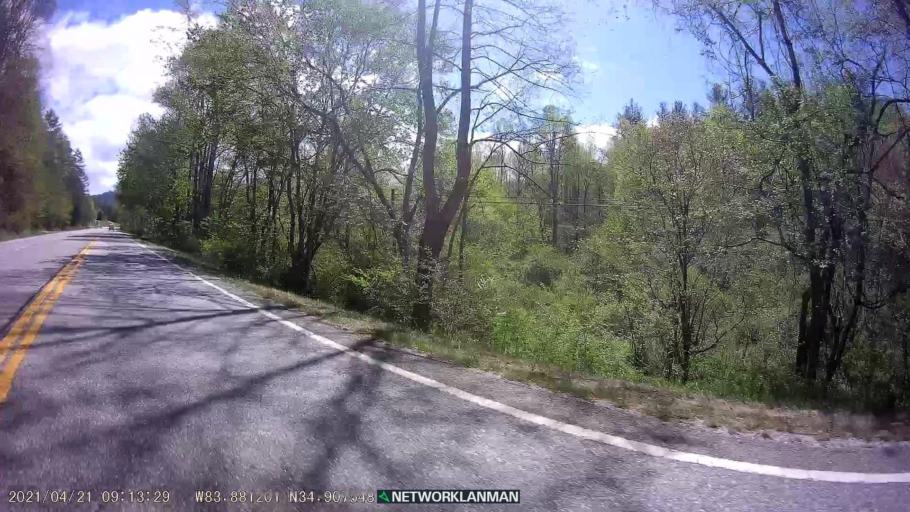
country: US
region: Georgia
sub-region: Union County
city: Blairsville
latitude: 34.9073
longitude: -83.8809
